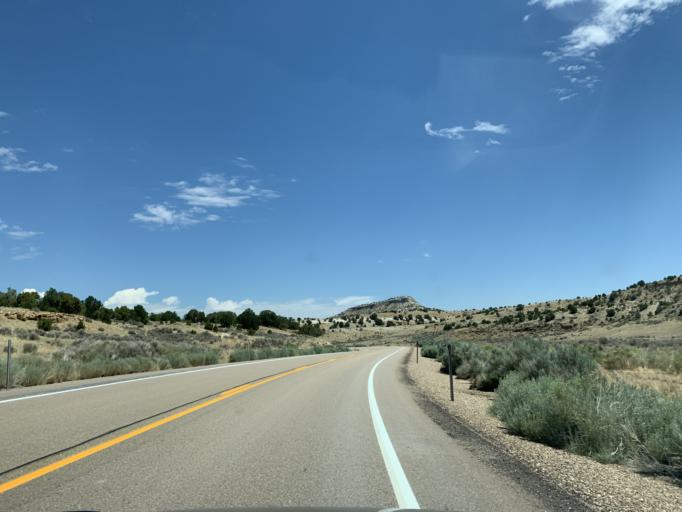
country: US
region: Utah
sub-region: Duchesne County
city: Duchesne
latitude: 39.9050
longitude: -110.2331
